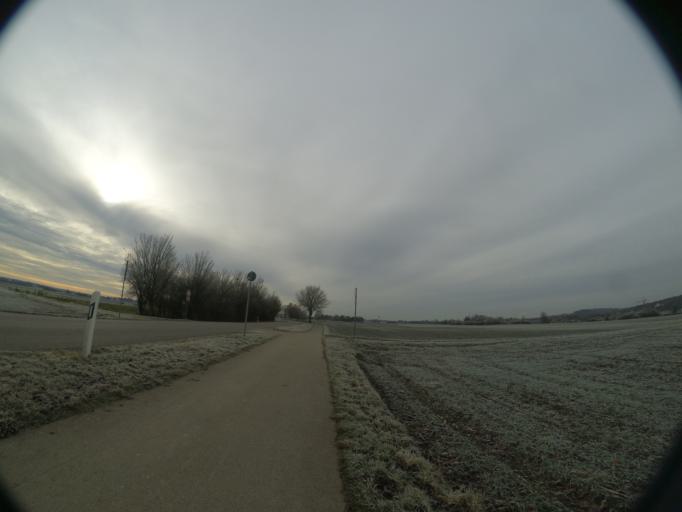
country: DE
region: Bavaria
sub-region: Swabia
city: Neu-Ulm
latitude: 48.4233
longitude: 10.0435
